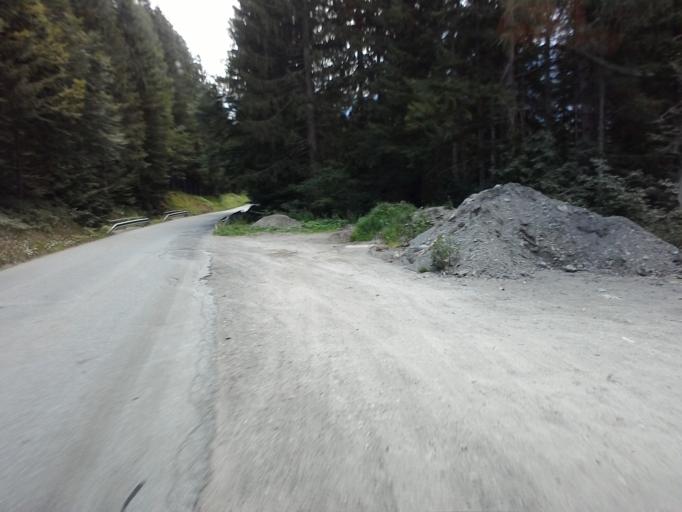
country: AT
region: Carinthia
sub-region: Politischer Bezirk Spittal an der Drau
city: Oberdrauburg
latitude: 46.6816
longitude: 12.9580
